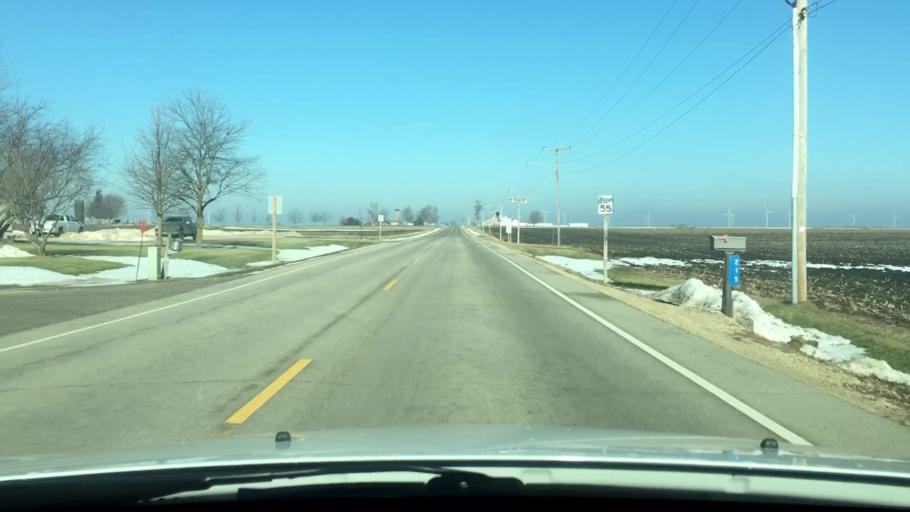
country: US
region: Illinois
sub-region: DeKalb County
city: Waterman
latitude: 41.7708
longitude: -88.8771
